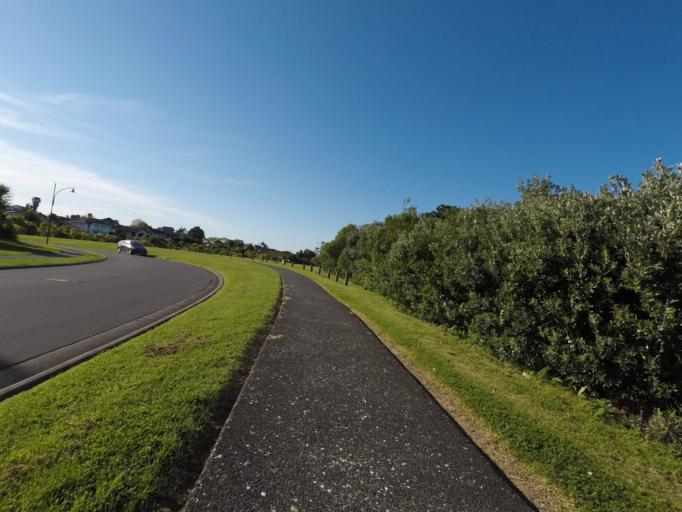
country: NZ
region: Auckland
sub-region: Auckland
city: Rosebank
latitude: -36.8343
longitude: 174.6619
